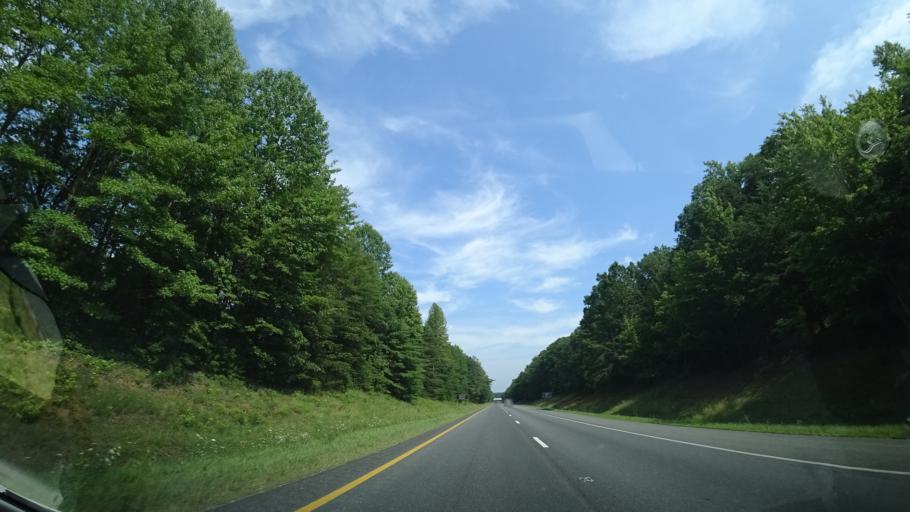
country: US
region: Virginia
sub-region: Louisa County
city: Louisa
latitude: 37.9364
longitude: -78.1009
